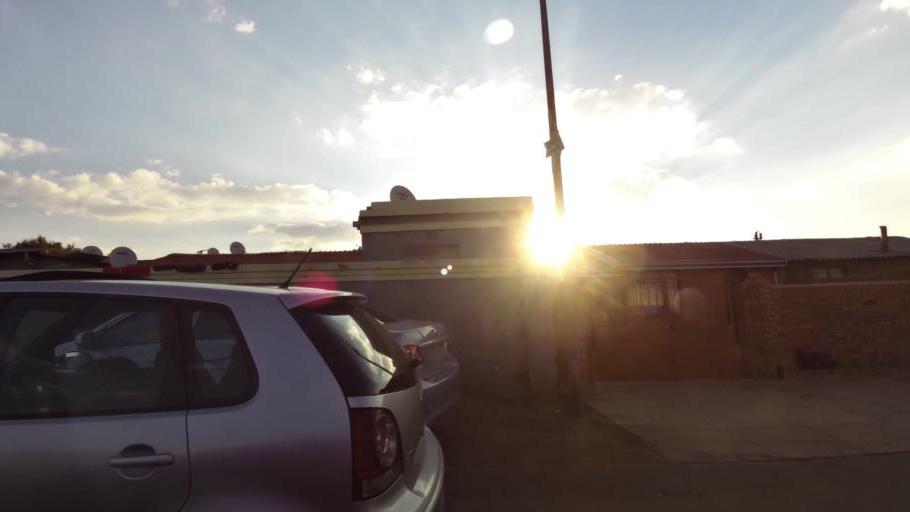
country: ZA
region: Gauteng
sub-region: City of Johannesburg Metropolitan Municipality
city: Roodepoort
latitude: -26.2119
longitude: 27.9013
